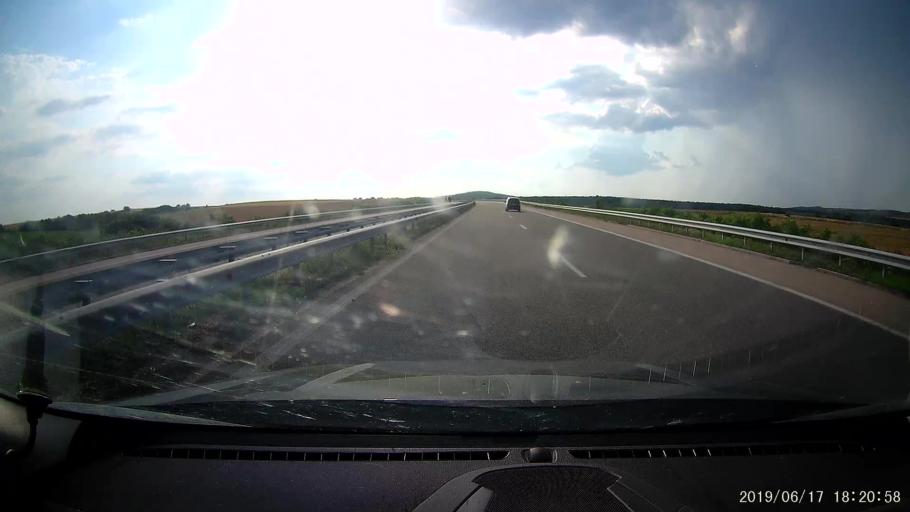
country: BG
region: Khaskovo
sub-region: Obshtina Simeonovgrad
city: Simeonovgrad
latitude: 41.9657
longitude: 25.7975
